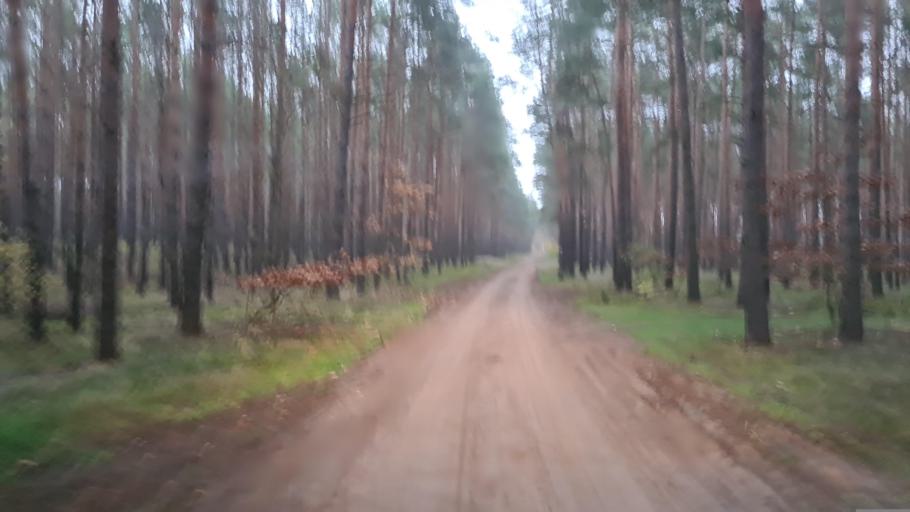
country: DE
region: Brandenburg
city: Beelitz
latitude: 52.2488
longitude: 13.0026
